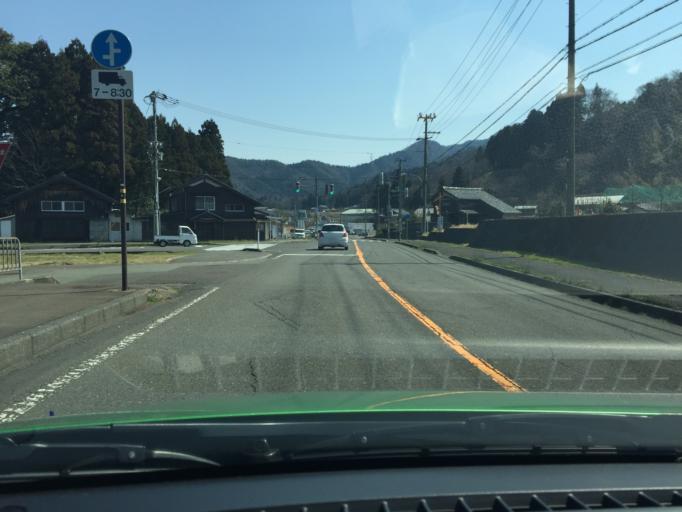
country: JP
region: Fukui
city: Obama
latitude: 35.4561
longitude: 135.7196
